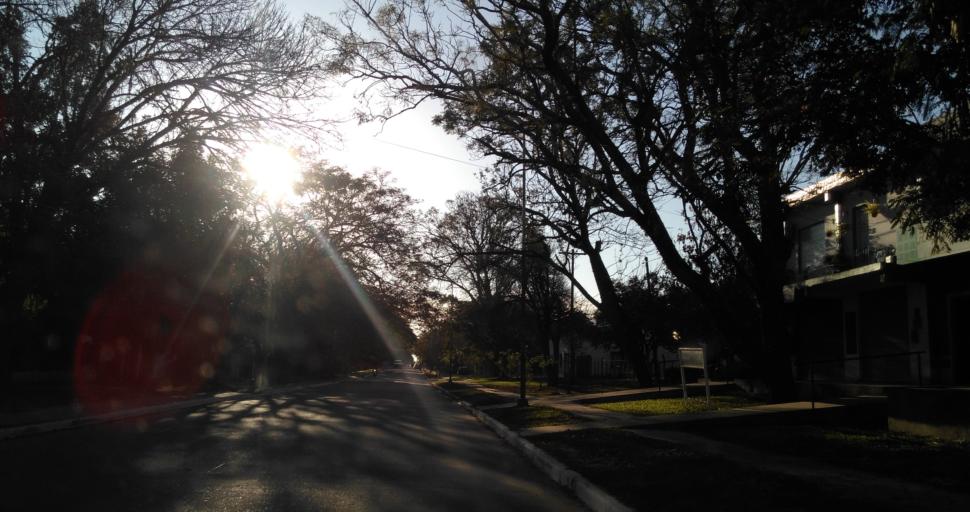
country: AR
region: Chaco
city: Colonia Benitez
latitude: -27.3310
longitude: -58.9484
